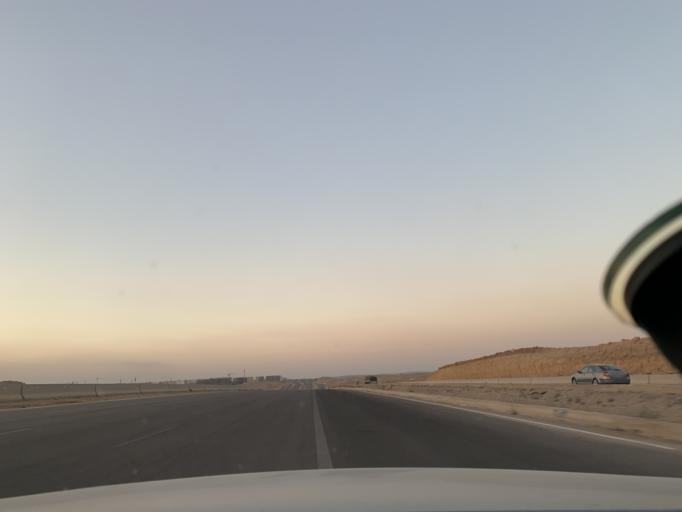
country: EG
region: Muhafazat al Qahirah
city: Halwan
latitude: 29.9535
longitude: 31.5406
